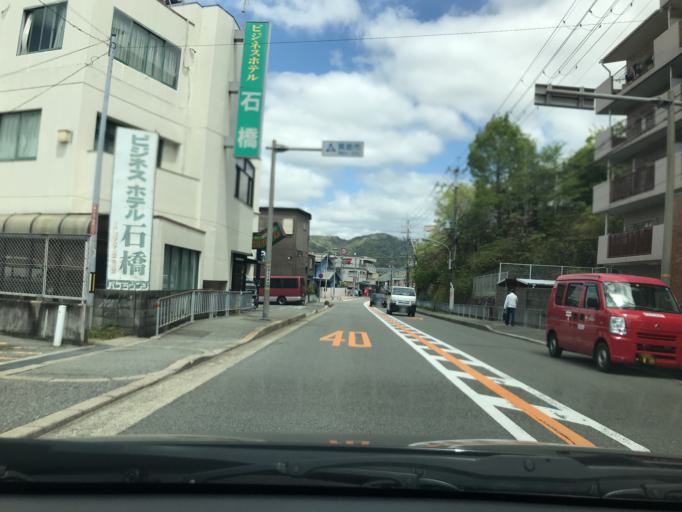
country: JP
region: Osaka
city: Ikeda
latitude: 34.8081
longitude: 135.4482
